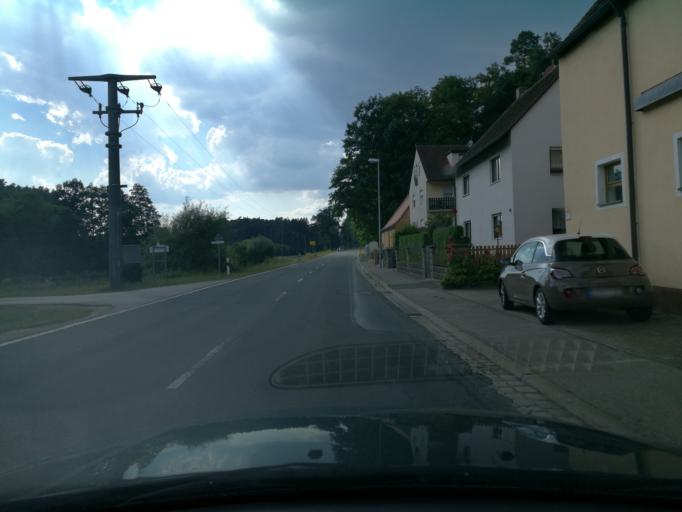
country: DE
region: Bavaria
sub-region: Regierungsbezirk Mittelfranken
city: Grosshabersdorf
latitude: 49.4116
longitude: 10.7586
